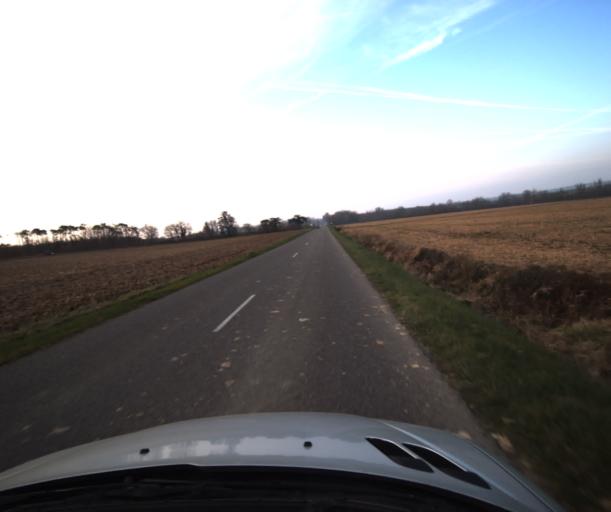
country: FR
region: Midi-Pyrenees
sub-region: Departement du Tarn-et-Garonne
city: Labastide-Saint-Pierre
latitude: 43.8948
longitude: 1.3721
